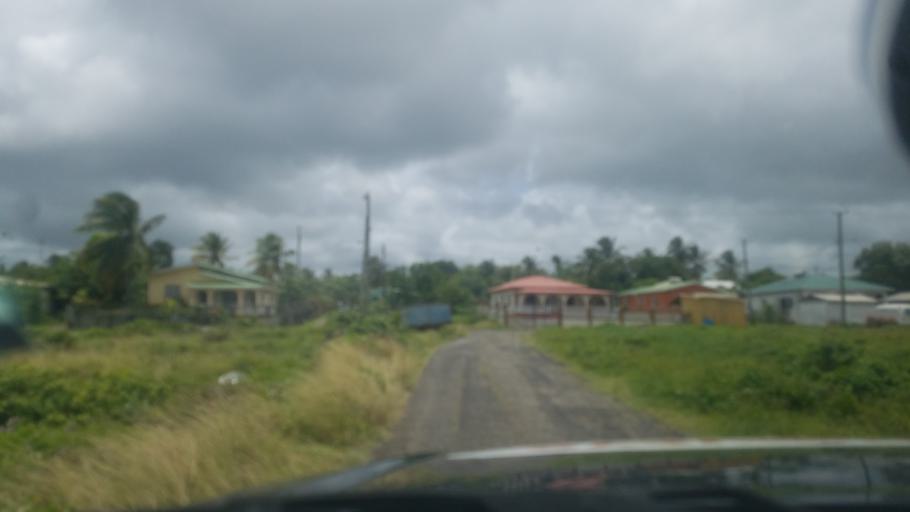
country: LC
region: Laborie Quarter
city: Laborie
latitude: 13.7551
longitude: -60.9739
